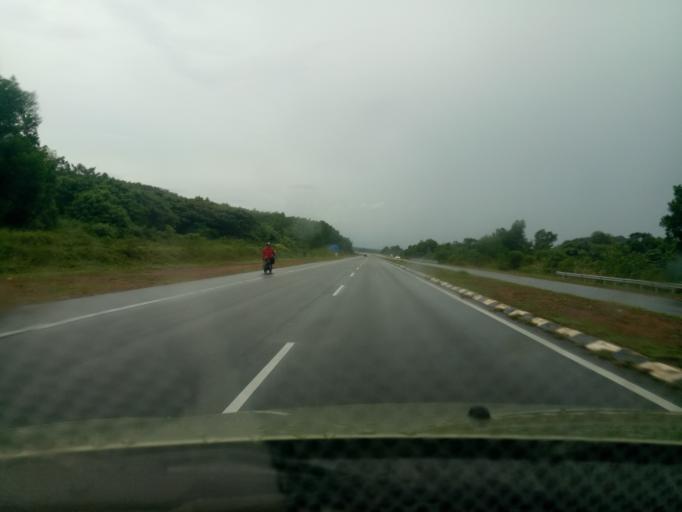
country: MY
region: Kedah
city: Sungai Petani
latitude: 5.6151
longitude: 100.5594
